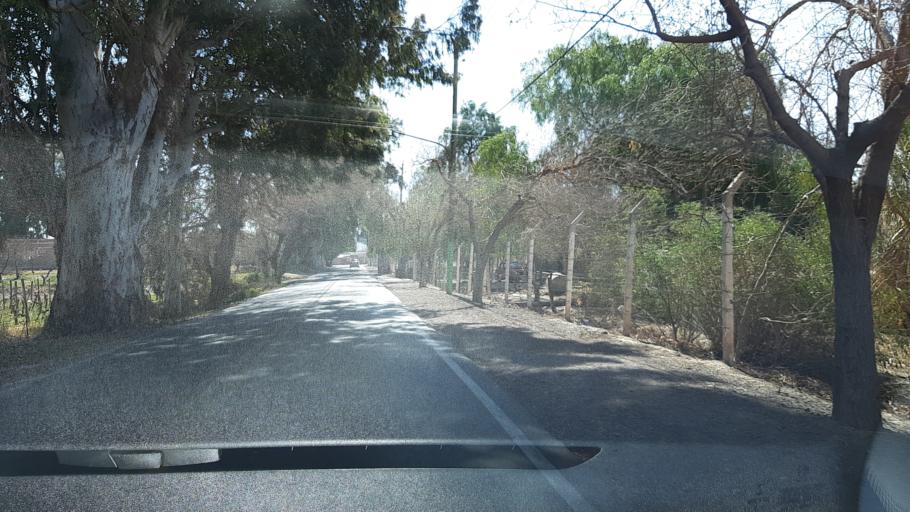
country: AR
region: San Juan
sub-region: Departamento de Rivadavia
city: Rivadavia
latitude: -31.5251
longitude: -68.6195
